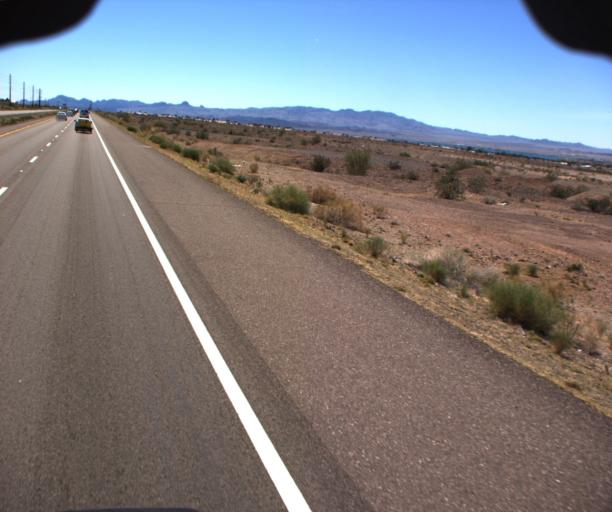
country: US
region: Arizona
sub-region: Mohave County
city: Desert Hills
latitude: 34.5589
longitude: -114.3598
